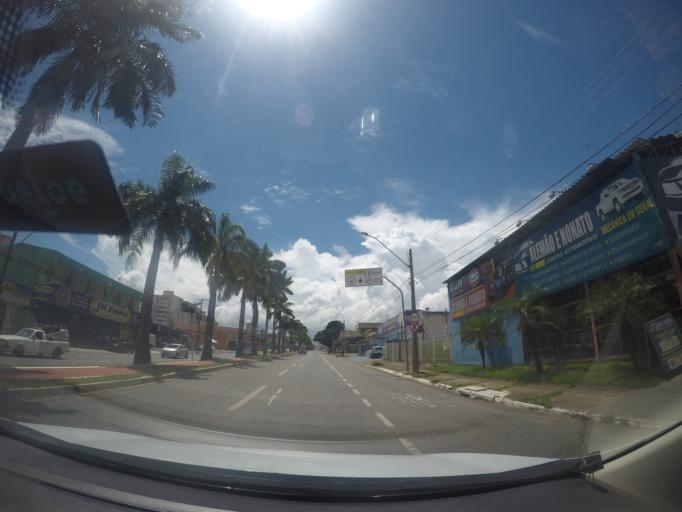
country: BR
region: Goias
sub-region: Goiania
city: Goiania
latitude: -16.7166
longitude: -49.2868
